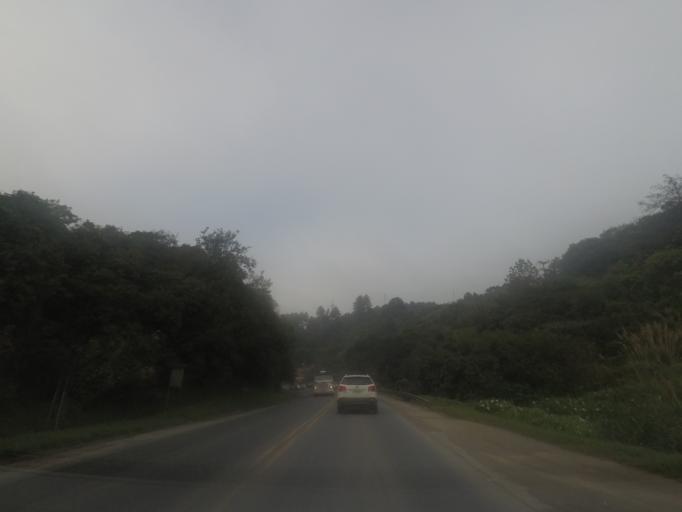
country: BR
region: Parana
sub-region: Almirante Tamandare
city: Almirante Tamandare
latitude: -25.3055
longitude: -49.3046
